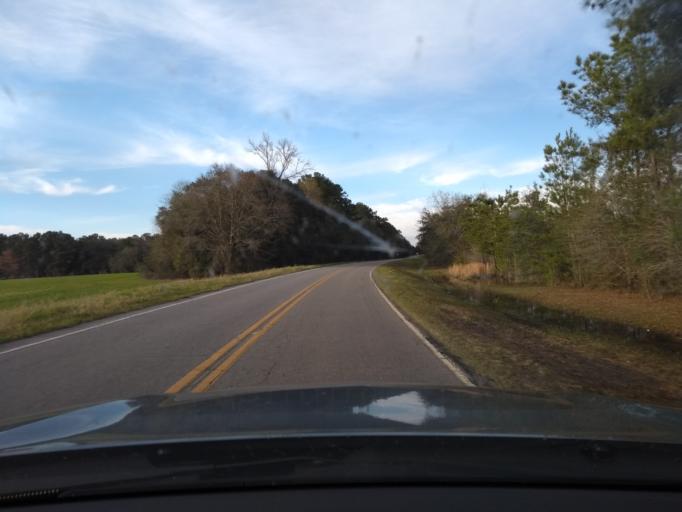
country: US
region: Georgia
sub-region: Evans County
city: Claxton
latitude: 32.2461
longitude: -81.7699
